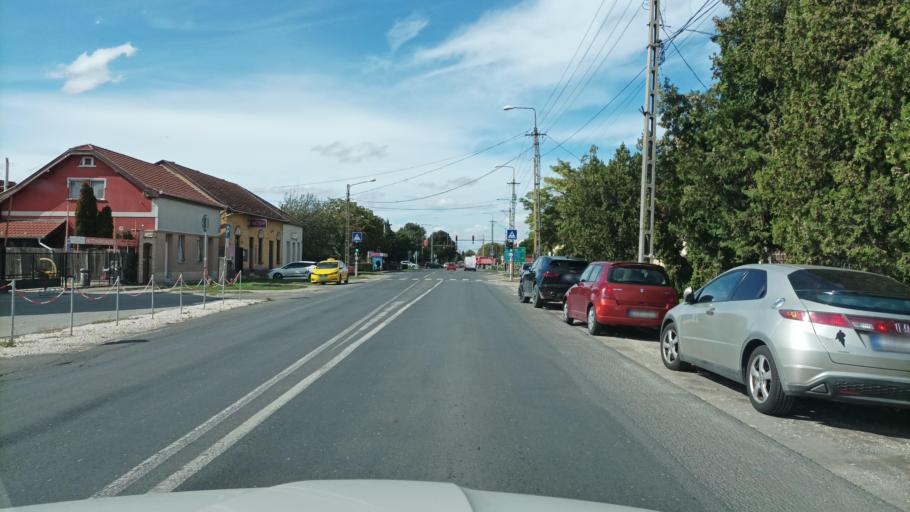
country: HU
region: Pest
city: Ullo
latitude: 47.3843
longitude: 19.3475
